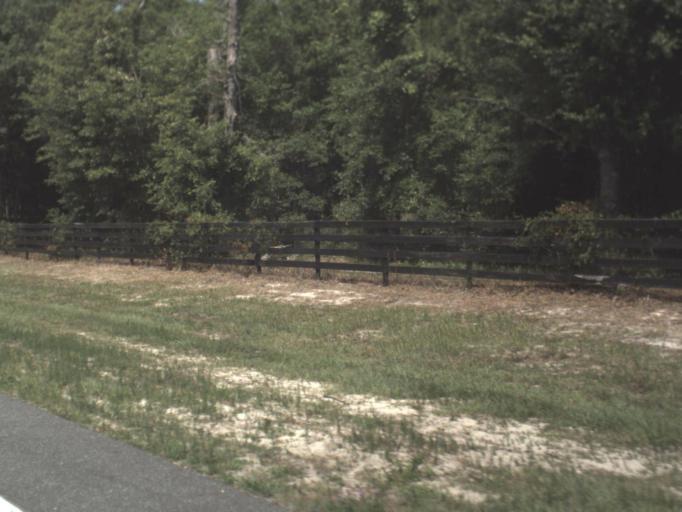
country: US
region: Florida
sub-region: Levy County
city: Williston
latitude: 29.4229
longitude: -82.4240
